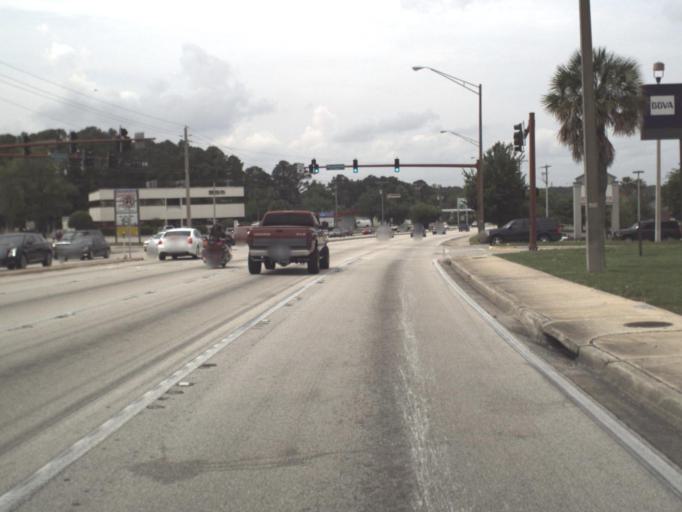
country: US
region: Florida
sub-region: Clay County
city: Bellair-Meadowbrook Terrace
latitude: 30.1551
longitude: -81.7480
